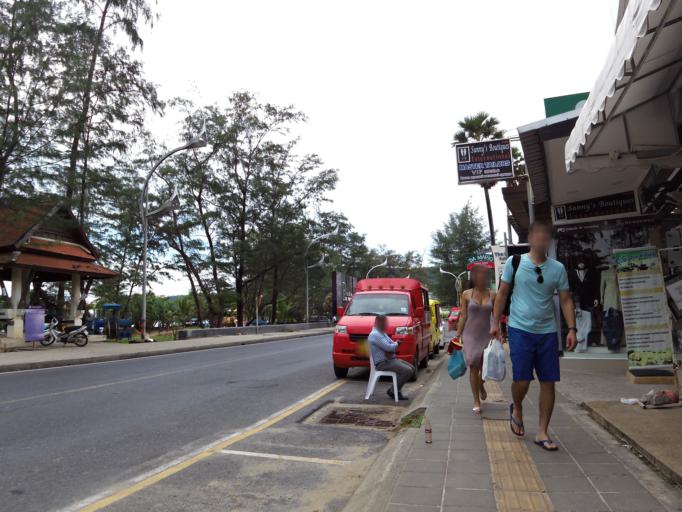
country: TH
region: Phuket
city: Ban Karon
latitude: 7.8476
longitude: 98.2935
